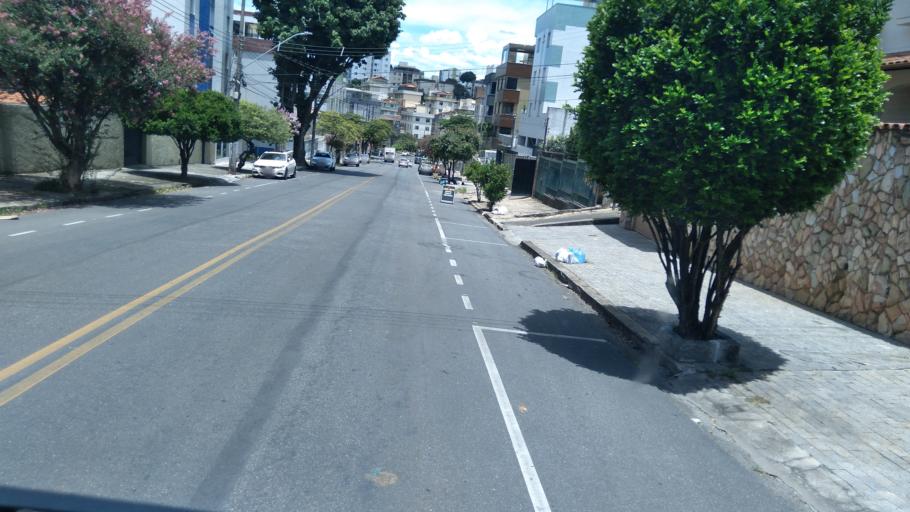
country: BR
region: Minas Gerais
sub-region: Belo Horizonte
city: Belo Horizonte
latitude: -19.9161
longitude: -43.9899
